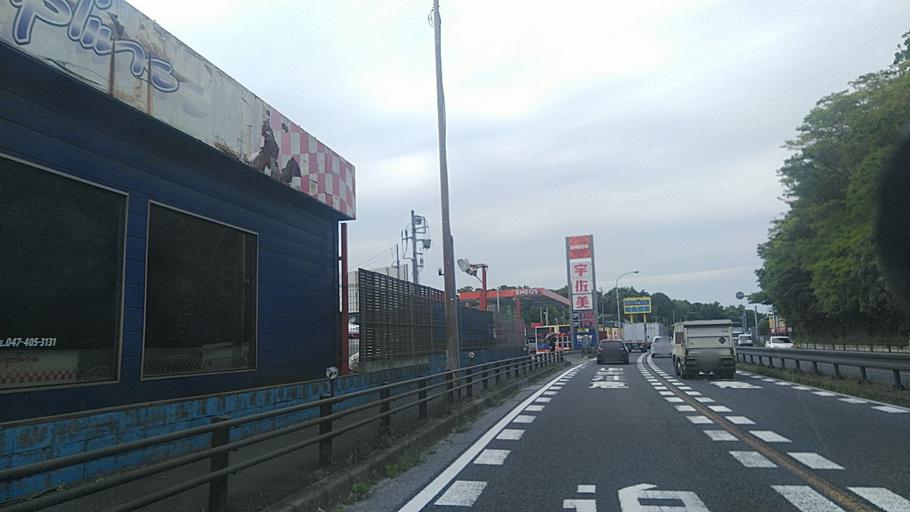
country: JP
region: Chiba
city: Yotsukaido
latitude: 35.6992
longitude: 140.1200
